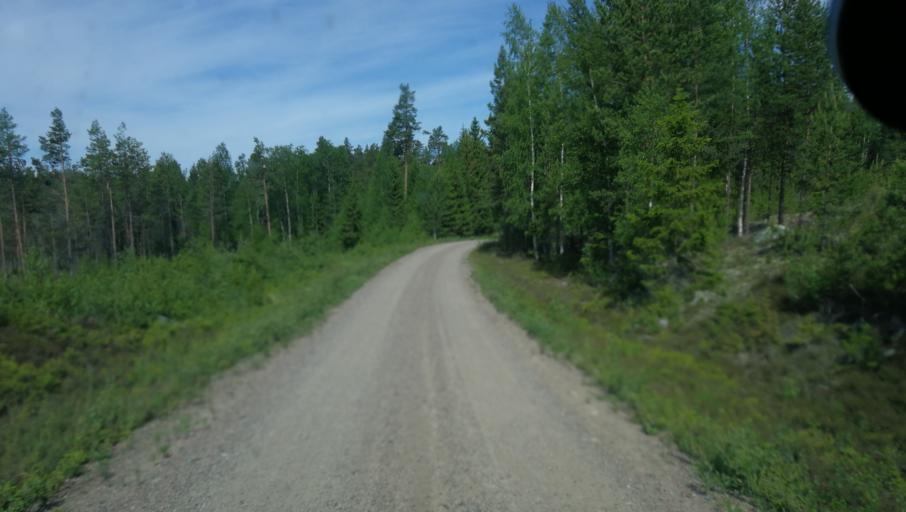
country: SE
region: Dalarna
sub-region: Vansbro Kommun
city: Vansbro
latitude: 60.8212
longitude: 14.1702
